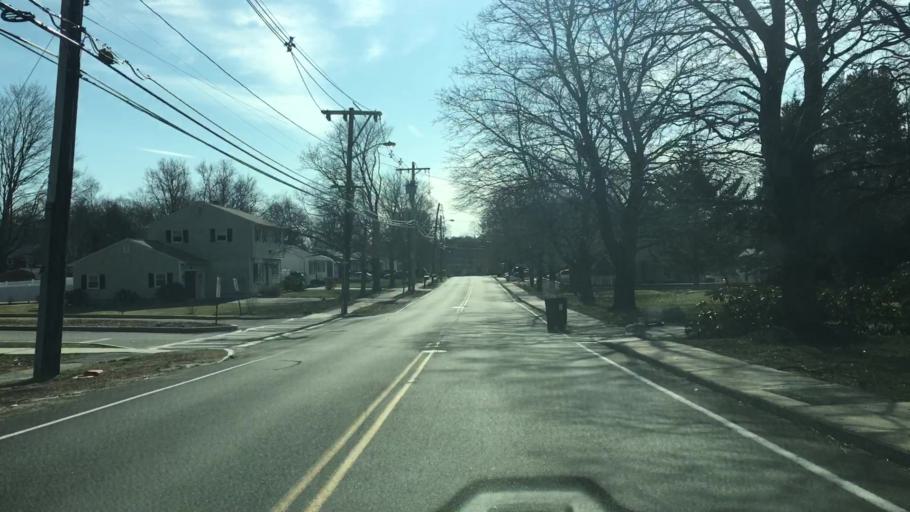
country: US
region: Massachusetts
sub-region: Essex County
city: Amesbury
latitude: 42.8550
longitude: -70.9498
